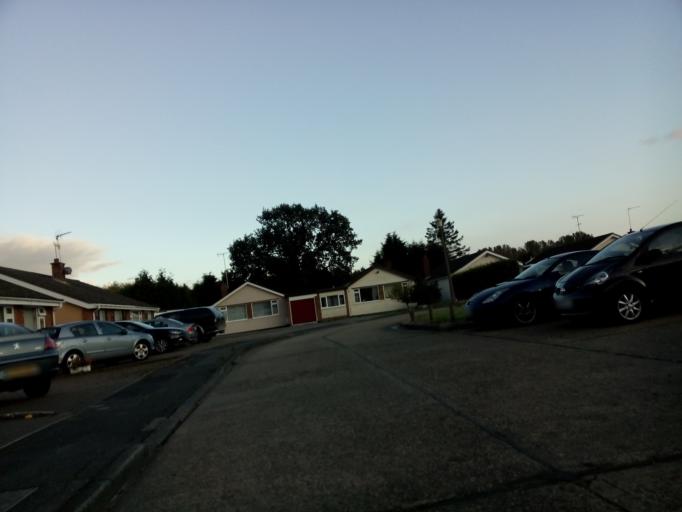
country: GB
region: England
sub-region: Suffolk
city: Bramford
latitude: 52.0607
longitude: 1.1038
